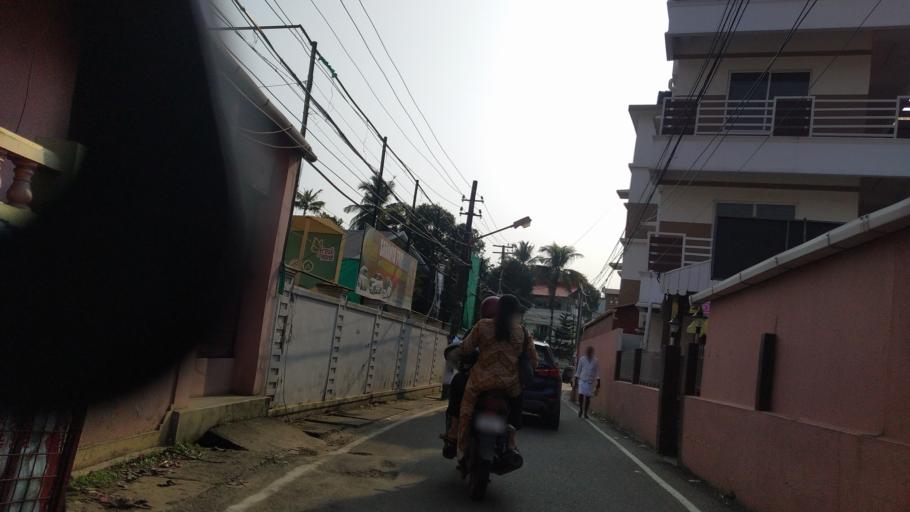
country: IN
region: Kerala
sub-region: Ernakulam
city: Cochin
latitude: 9.9983
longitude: 76.2929
